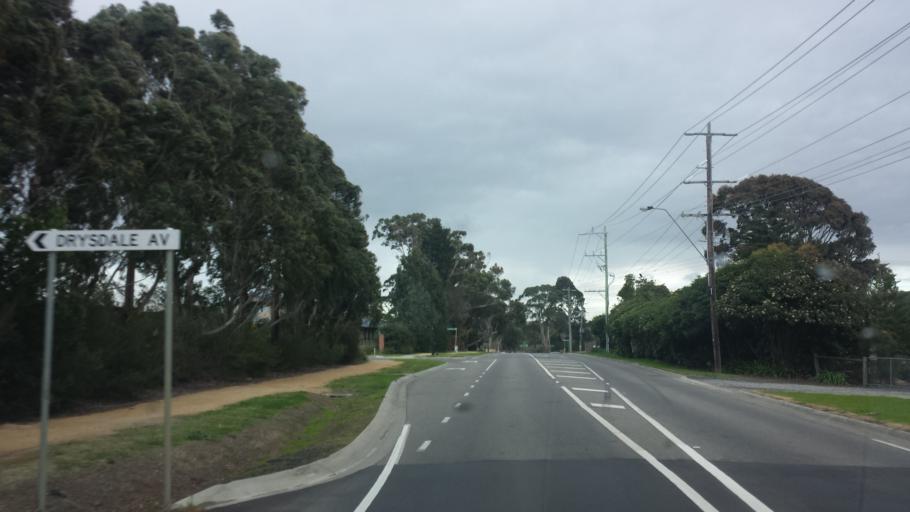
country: AU
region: Victoria
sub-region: Casey
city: Narre Warren North
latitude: -37.9905
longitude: 145.2930
